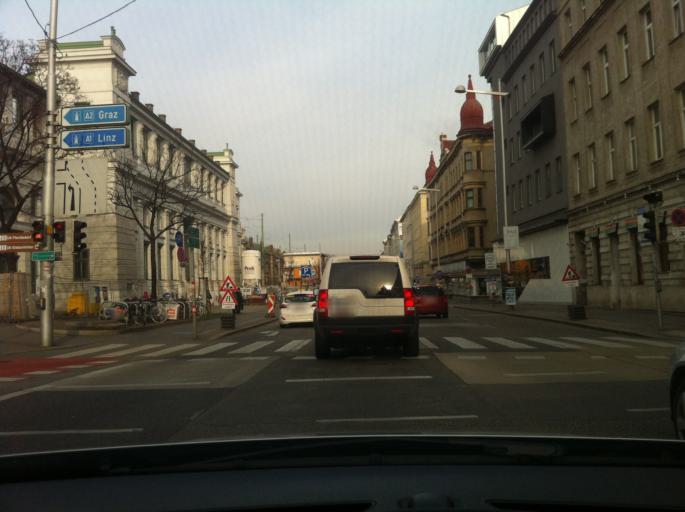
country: AT
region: Vienna
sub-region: Wien Stadt
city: Vienna
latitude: 48.2250
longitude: 16.3498
